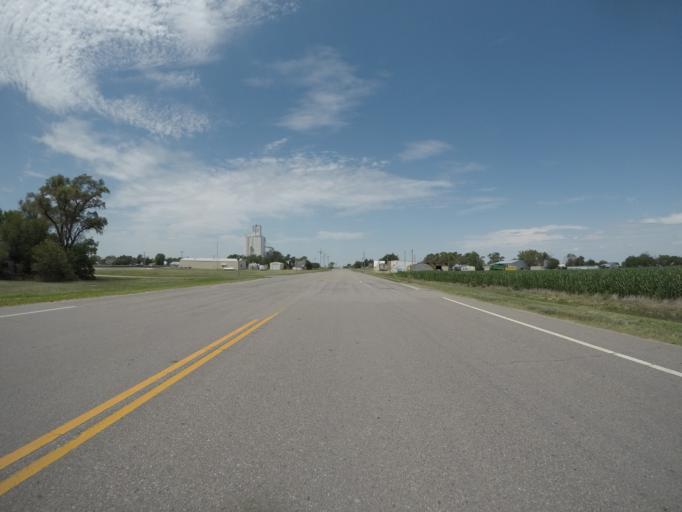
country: US
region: Kansas
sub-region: Rooks County
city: Stockton
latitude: 39.4560
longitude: -99.0981
